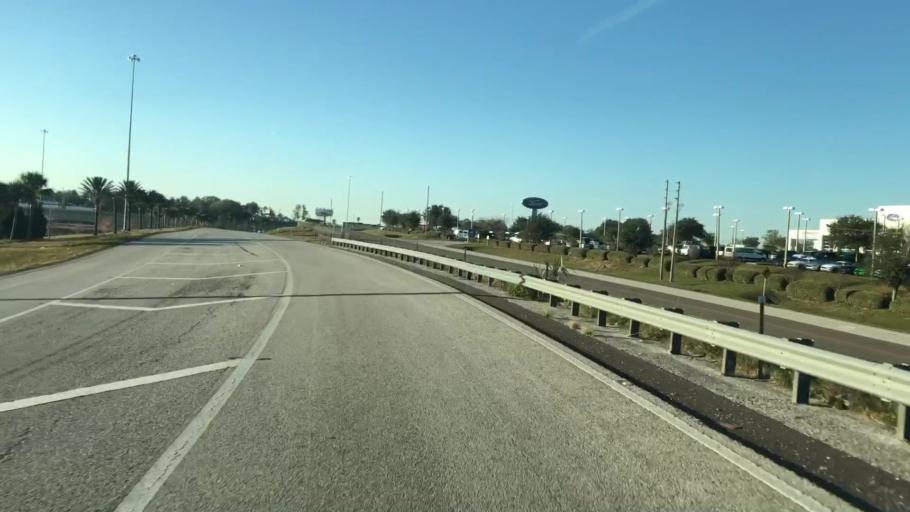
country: US
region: Florida
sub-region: Polk County
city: Loughman
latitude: 28.2336
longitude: -81.6540
